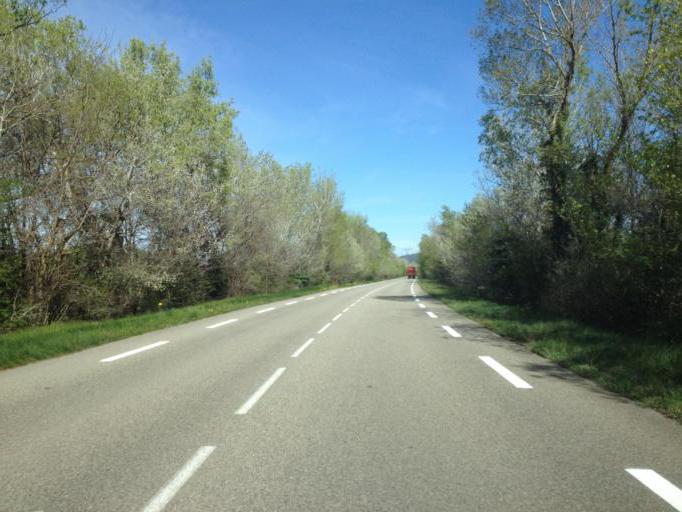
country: FR
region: Provence-Alpes-Cote d'Azur
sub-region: Departement du Vaucluse
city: Caderousse
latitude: 44.1161
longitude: 4.7220
